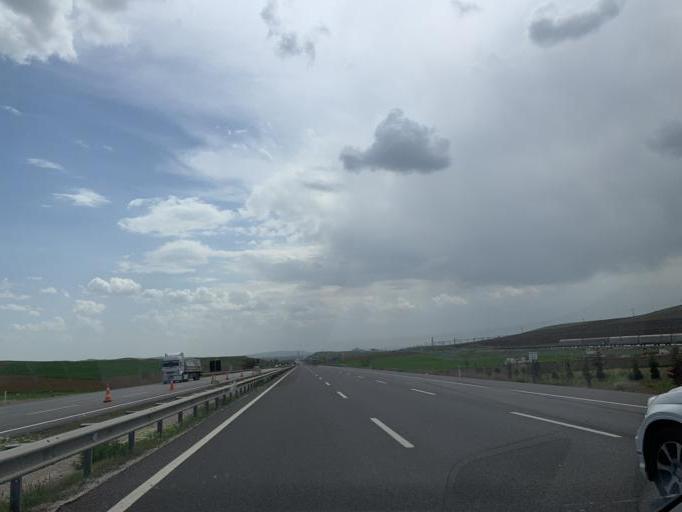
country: TR
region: Ankara
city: Polatli
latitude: 39.6135
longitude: 32.1855
